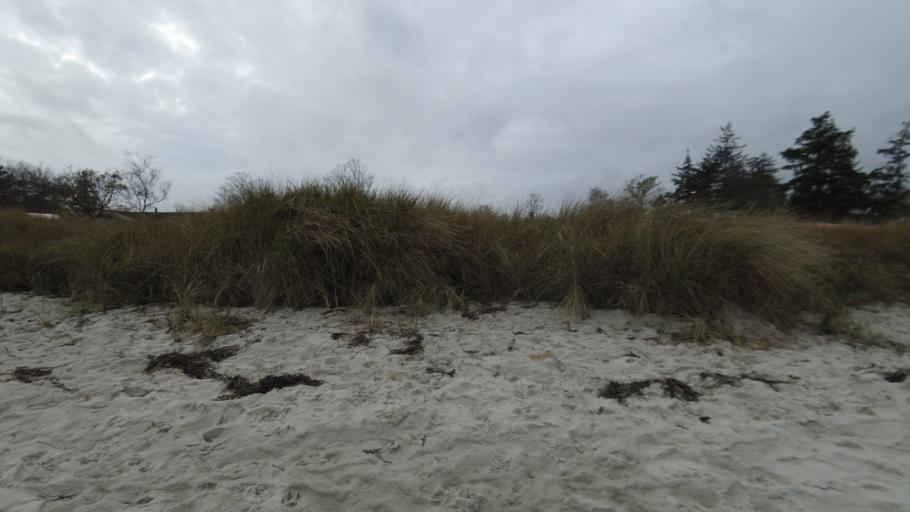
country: DK
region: Central Jutland
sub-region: Arhus Kommune
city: Malling
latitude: 55.9791
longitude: 10.2529
